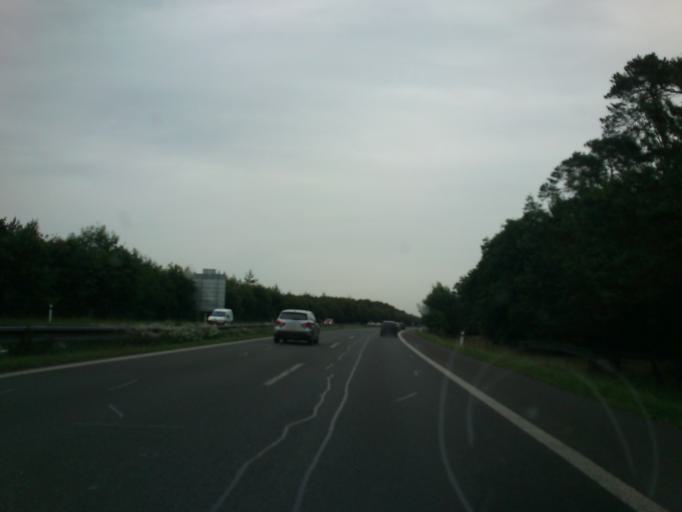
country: CZ
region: Central Bohemia
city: Brandys nad Labem-Stara Boleslav
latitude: 50.2111
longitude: 14.6999
